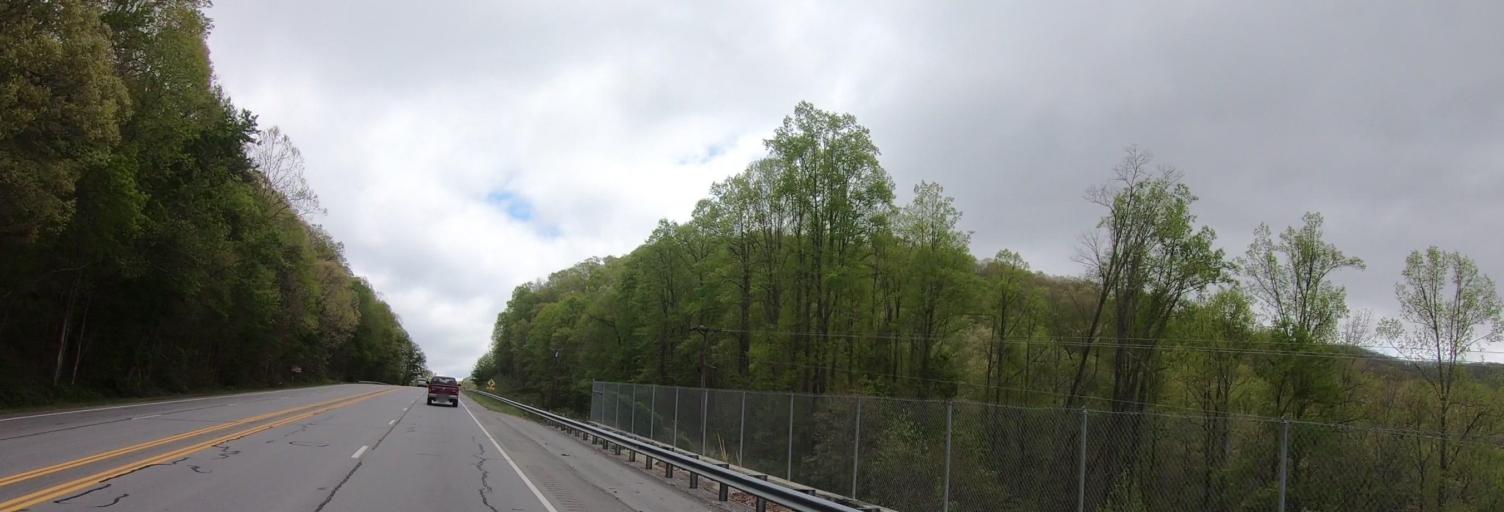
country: US
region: Georgia
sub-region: Towns County
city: Hiawassee
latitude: 34.9659
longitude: -83.8381
